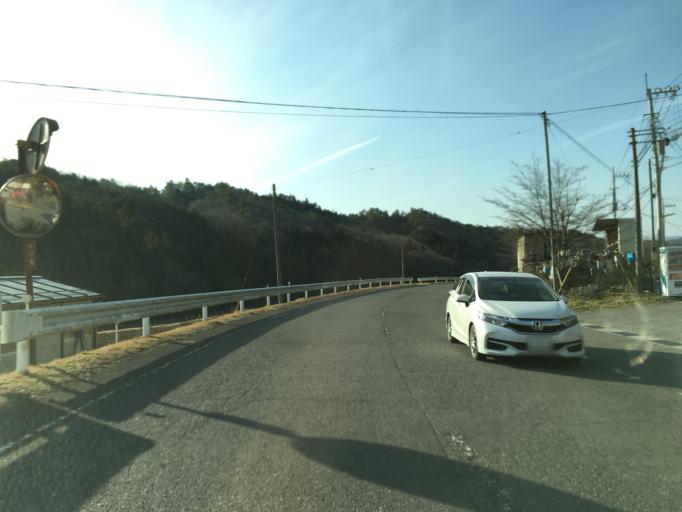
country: JP
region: Ibaraki
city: Daigo
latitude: 36.7514
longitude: 140.4422
